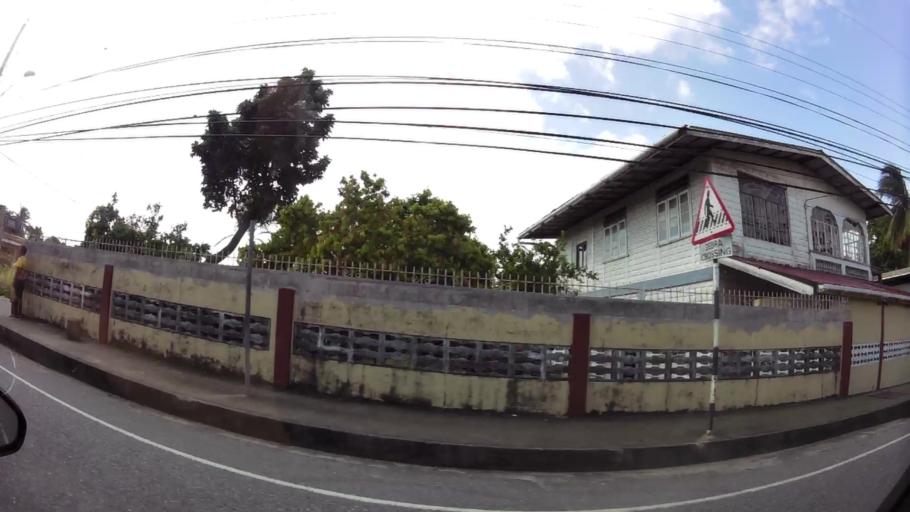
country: TT
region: Borough of Arima
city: Arima
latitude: 10.6326
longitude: -61.2760
